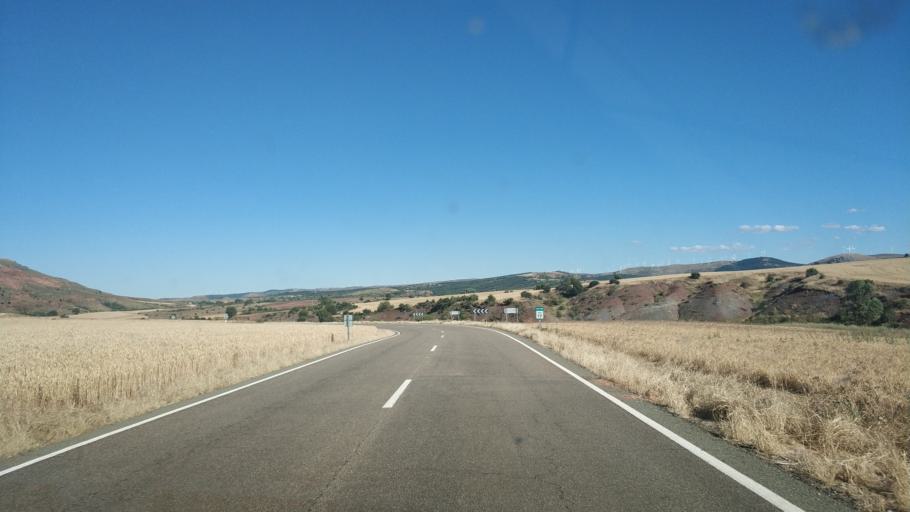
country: ES
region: Castille and Leon
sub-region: Provincia de Soria
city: Montejo de Tiermes
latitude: 41.3485
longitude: -3.1606
